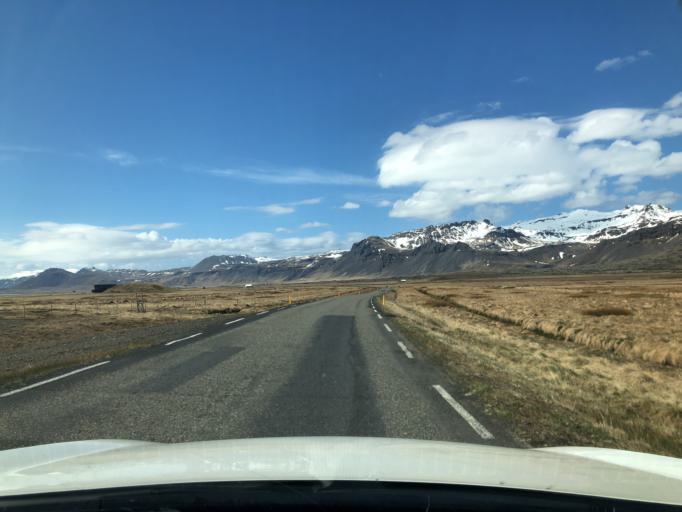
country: IS
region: West
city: Olafsvik
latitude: 64.8252
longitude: -23.2200
